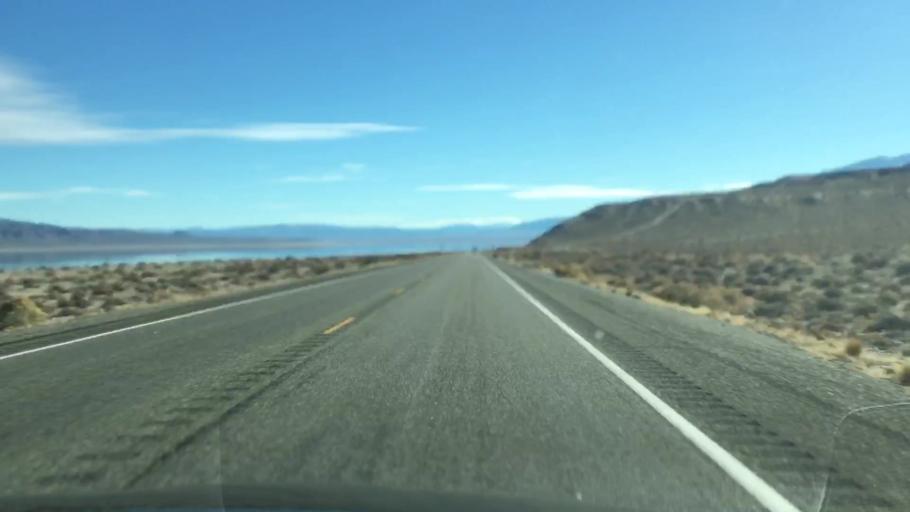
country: US
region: Nevada
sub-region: Mineral County
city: Hawthorne
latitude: 38.7888
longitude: -118.7543
